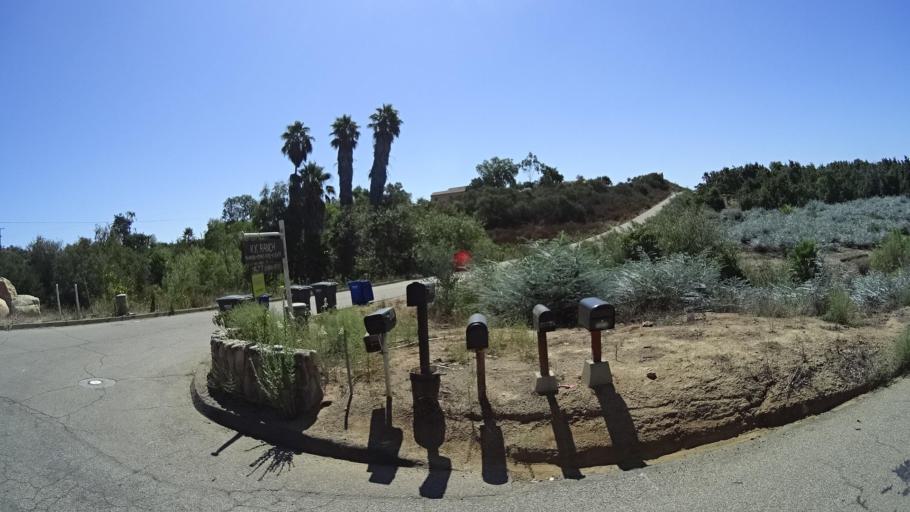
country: US
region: California
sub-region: San Diego County
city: Hidden Meadows
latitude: 33.2410
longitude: -117.0804
